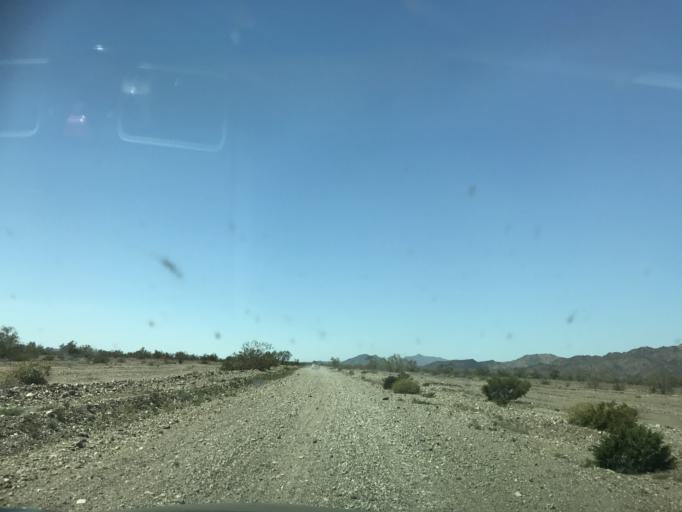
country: US
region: California
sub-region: Riverside County
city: Mesa Verde
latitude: 33.4807
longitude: -114.9292
